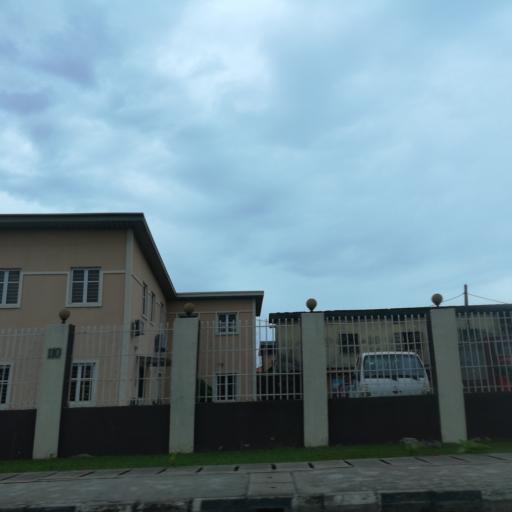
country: NG
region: Lagos
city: Ebute Metta
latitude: 6.4865
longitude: 3.3812
